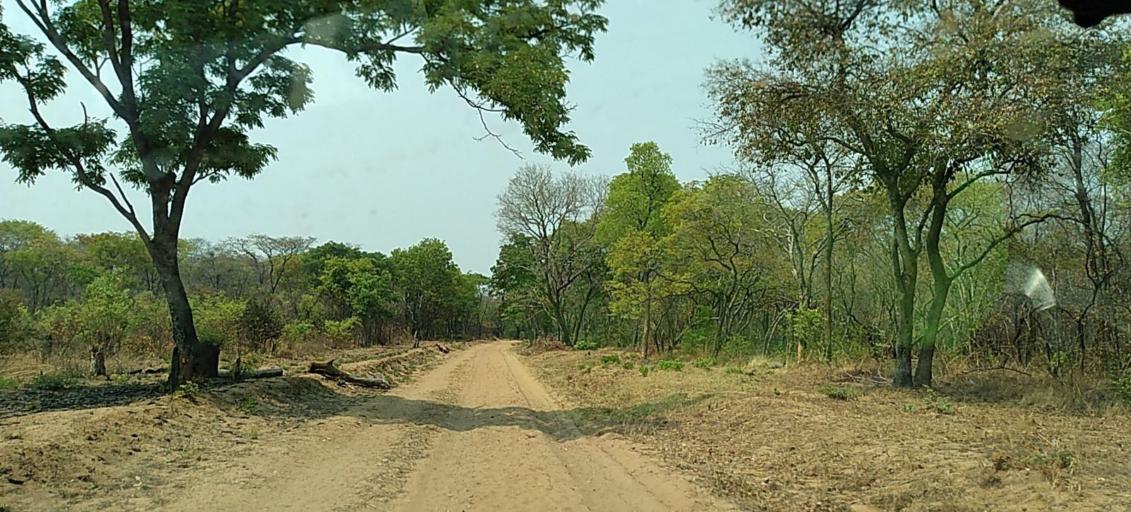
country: ZM
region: Western
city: Lukulu
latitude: -13.9909
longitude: 23.2315
